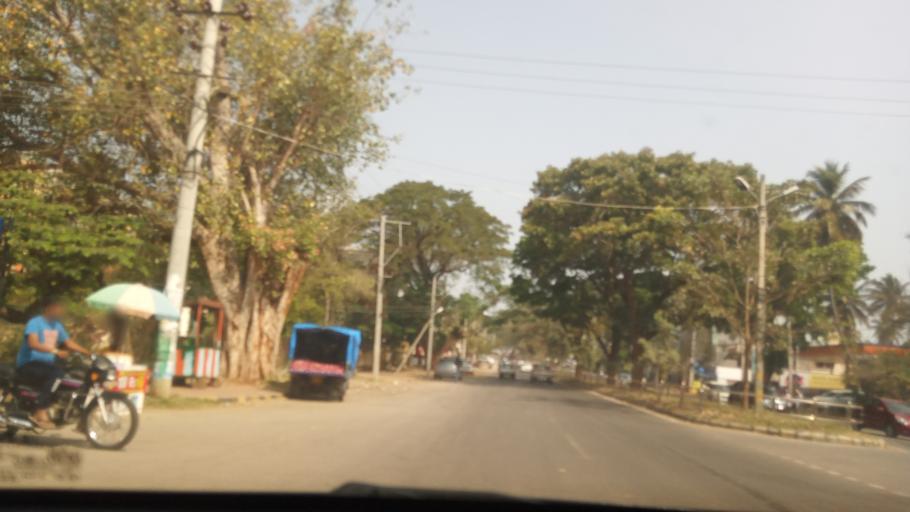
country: IN
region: Karnataka
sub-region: Mysore
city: Mysore
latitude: 12.2977
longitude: 76.6259
